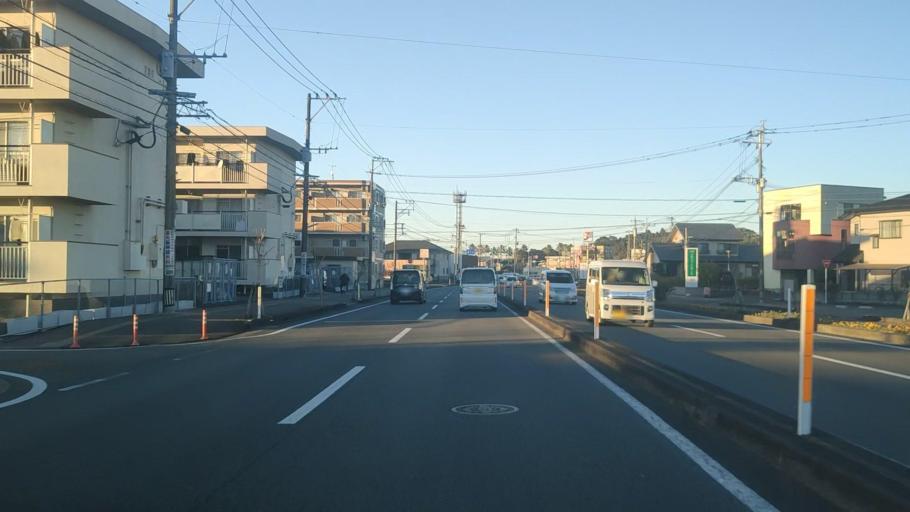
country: JP
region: Miyazaki
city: Miyazaki-shi
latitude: 31.8997
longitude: 131.4059
